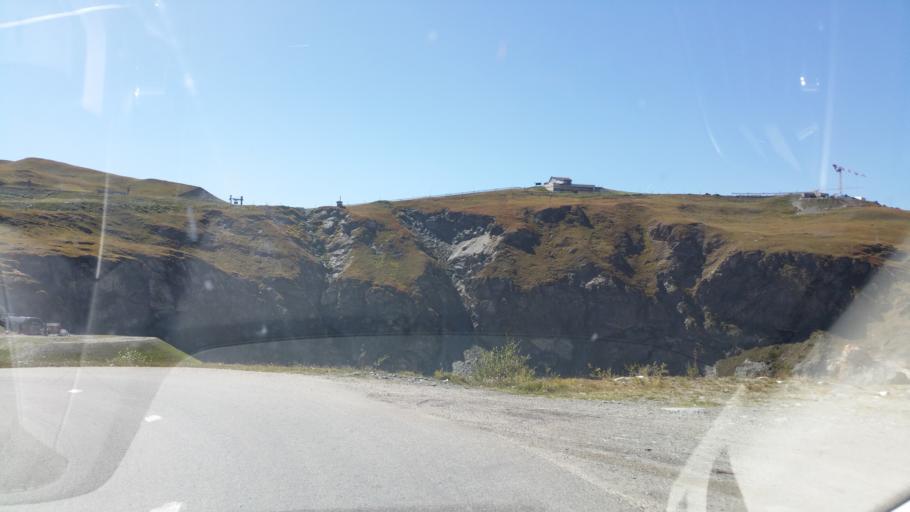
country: FR
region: Rhone-Alpes
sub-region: Departement de la Savoie
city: Val-d'Isere
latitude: 45.4337
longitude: 7.0035
